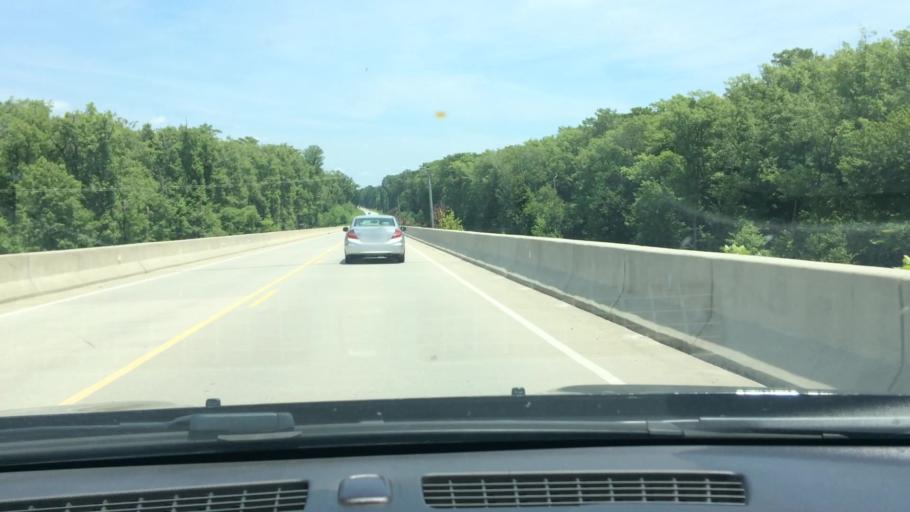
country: US
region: North Carolina
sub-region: Beaufort County
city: Washington
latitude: 35.5753
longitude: -77.1750
